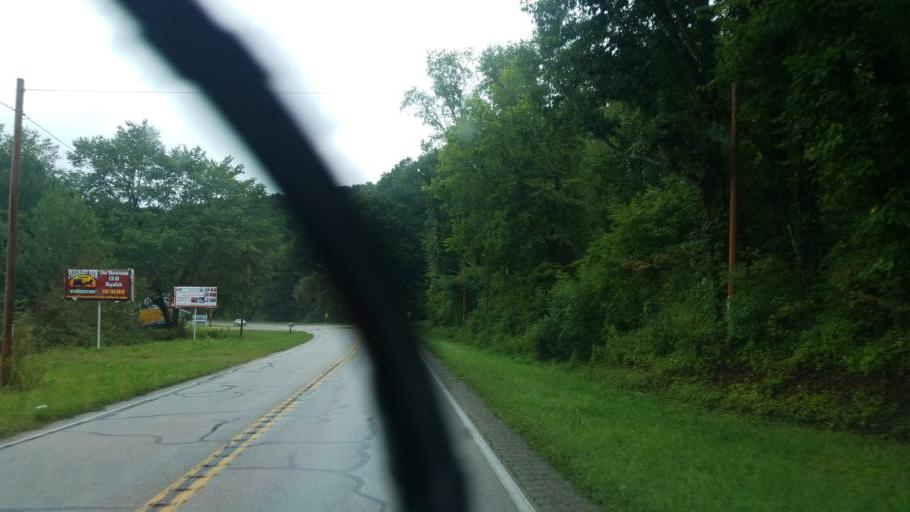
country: US
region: Kentucky
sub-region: Rowan County
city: Morehead
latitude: 38.1531
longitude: -83.4932
